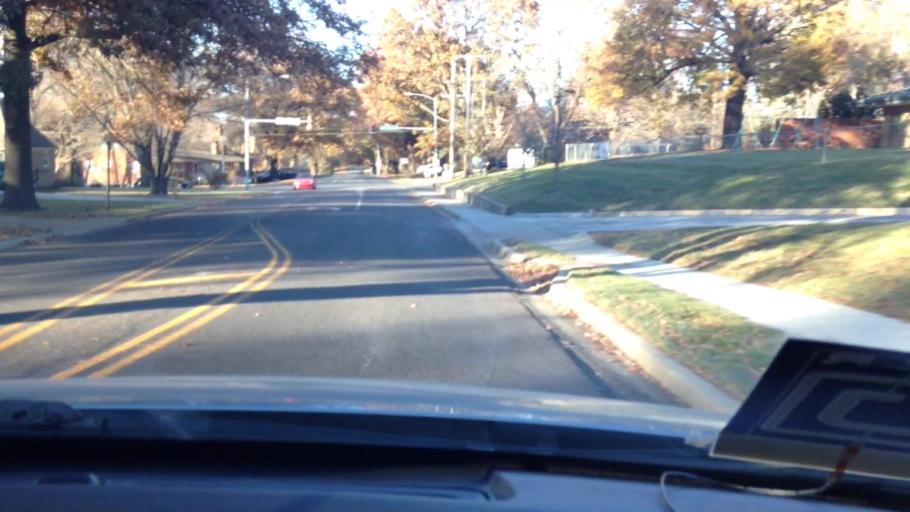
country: US
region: Kansas
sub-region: Johnson County
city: Overland Park
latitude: 38.9777
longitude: -94.6583
